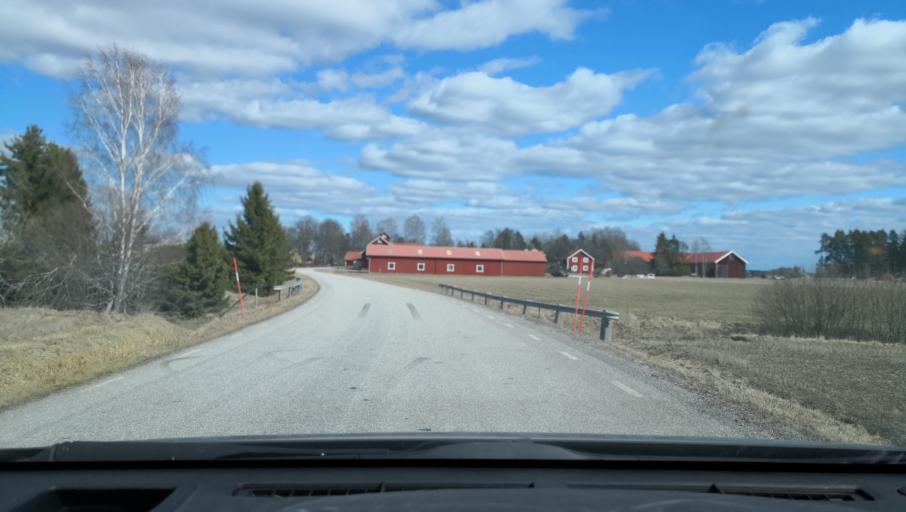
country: SE
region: Vaestmanland
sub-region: Sala Kommun
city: Sala
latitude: 59.8588
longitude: 16.6160
